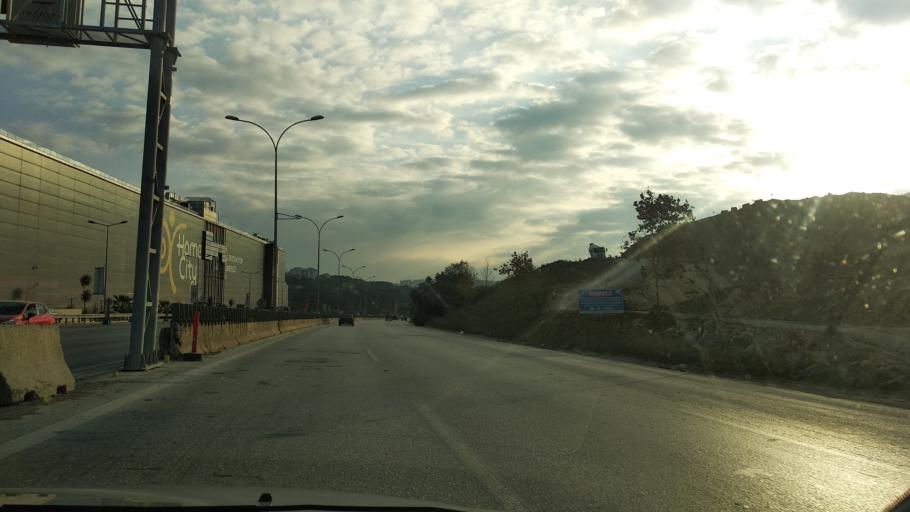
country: TR
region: Istanbul
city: Icmeler
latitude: 40.8887
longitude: 29.3248
